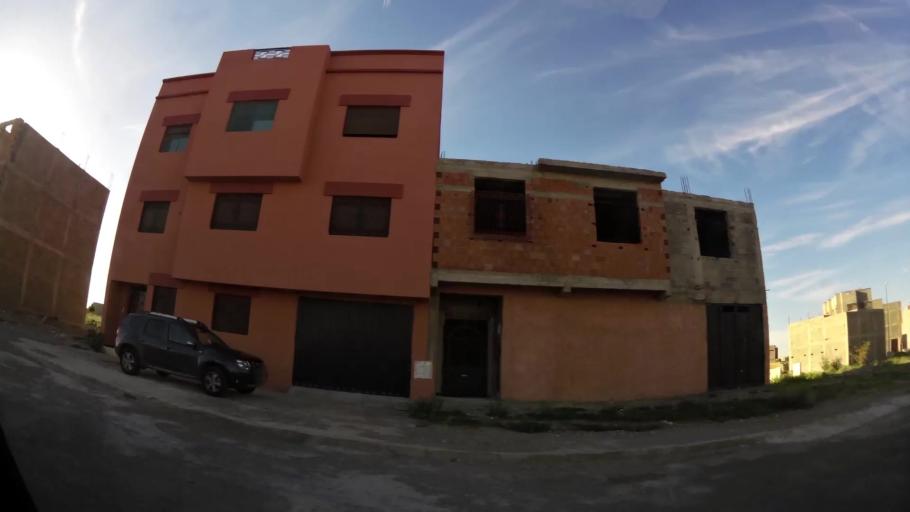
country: MA
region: Marrakech-Tensift-Al Haouz
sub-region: Marrakech
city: Marrakesh
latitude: 31.7664
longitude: -8.1037
